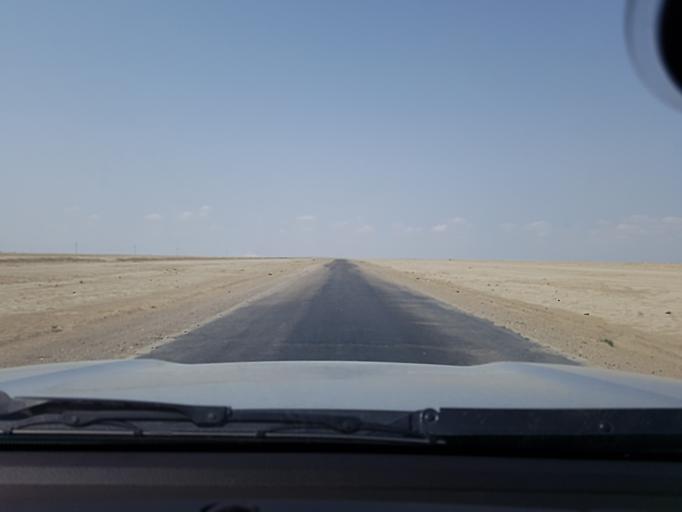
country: TM
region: Balkan
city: Gumdag
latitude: 38.6807
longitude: 54.4158
